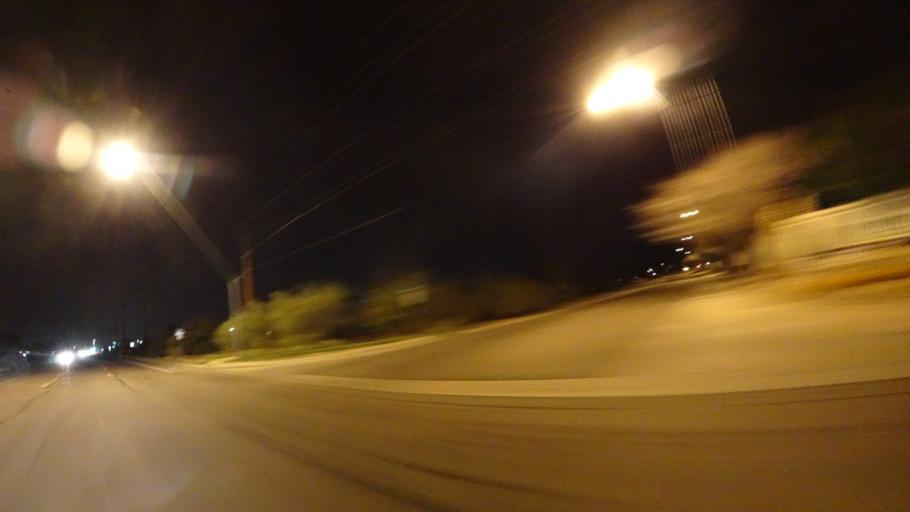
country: US
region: Arizona
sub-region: Pinal County
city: Apache Junction
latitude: 33.4224
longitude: -111.6500
